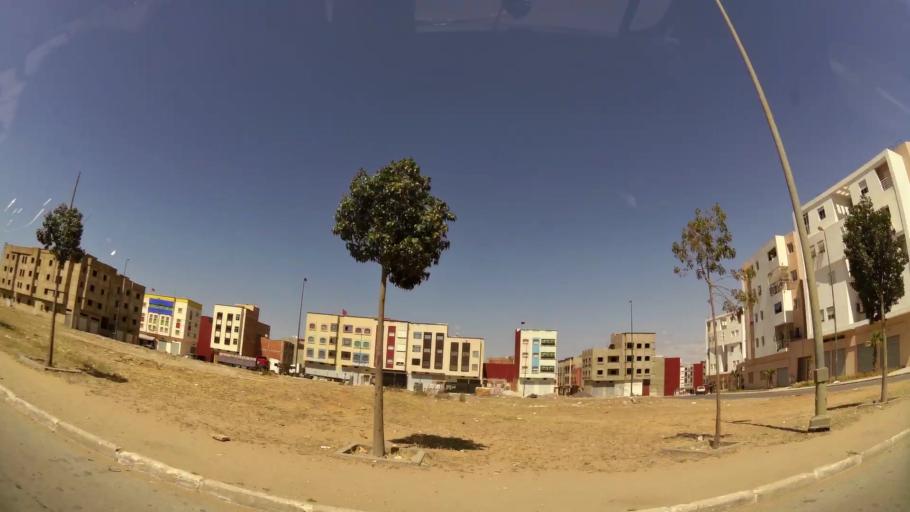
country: MA
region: Gharb-Chrarda-Beni Hssen
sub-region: Kenitra Province
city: Kenitra
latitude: 34.2391
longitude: -6.5465
